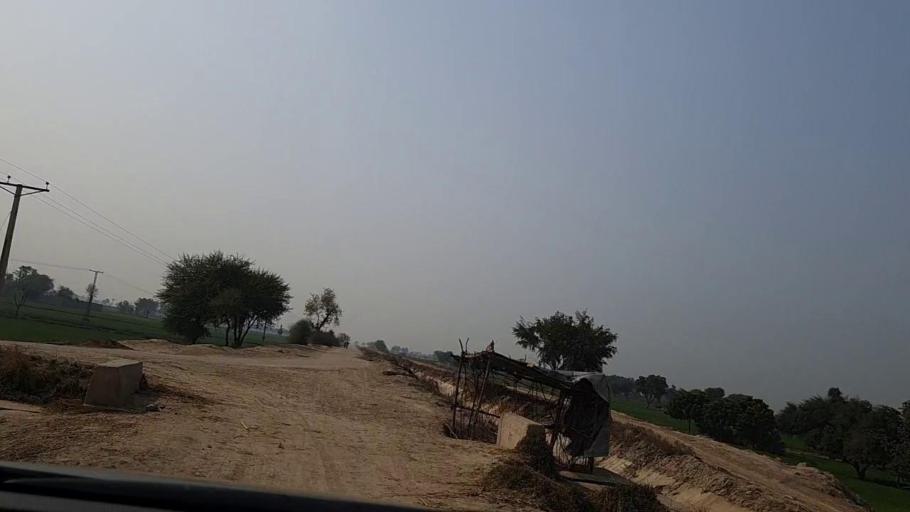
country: PK
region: Sindh
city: Sakrand
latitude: 26.1390
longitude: 68.2257
